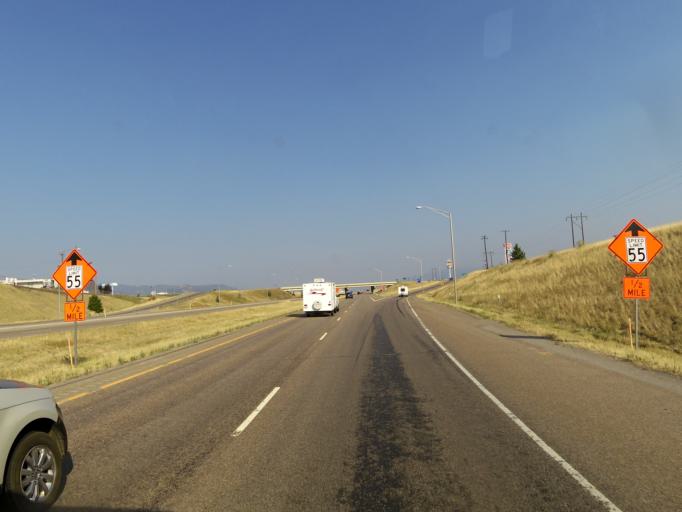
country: US
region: Montana
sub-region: Missoula County
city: Orchard Homes
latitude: 46.9494
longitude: -114.1276
